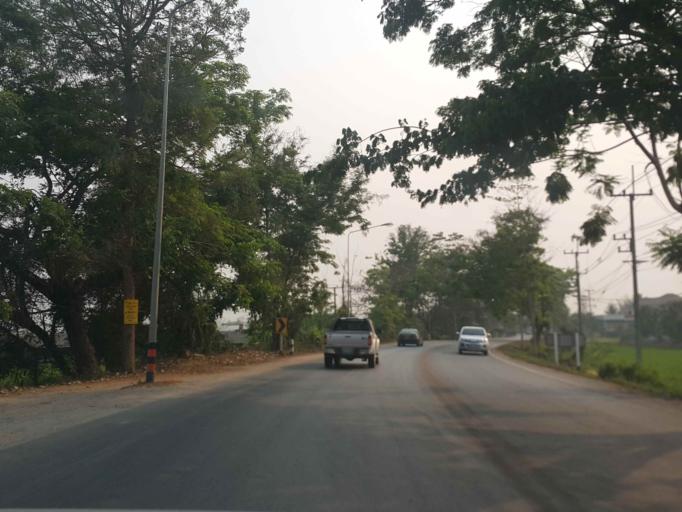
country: TH
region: Chiang Mai
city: Mae Taeng
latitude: 19.0351
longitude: 98.9685
